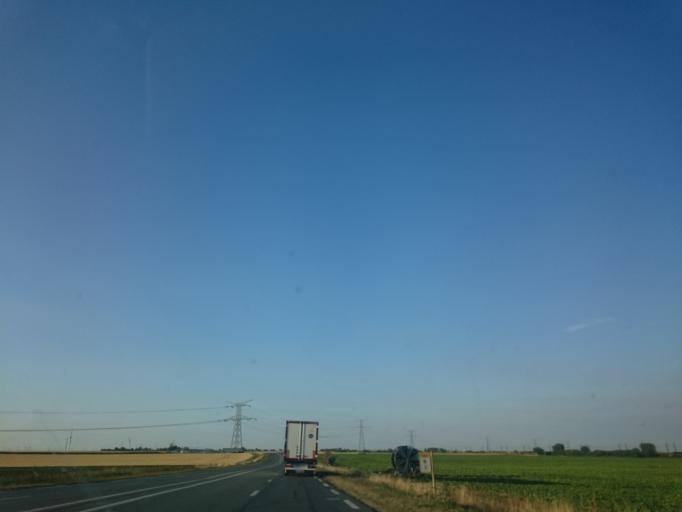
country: FR
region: Centre
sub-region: Departement du Loiret
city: Artenay
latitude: 48.1270
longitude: 1.8994
